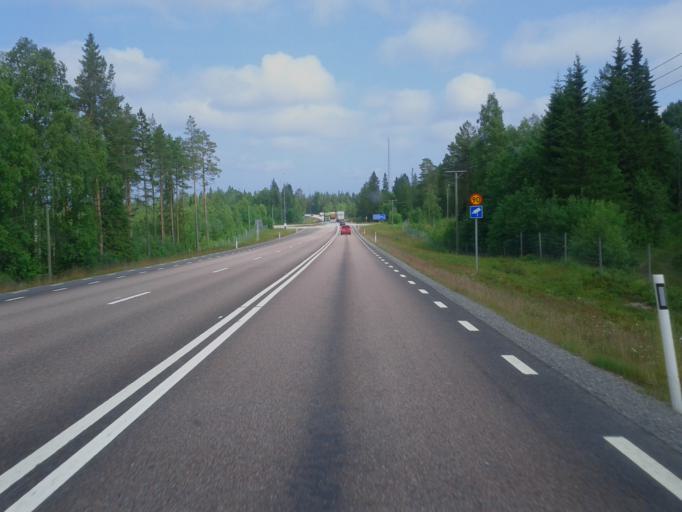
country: SE
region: Vaesterbotten
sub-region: Skelleftea Kommun
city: Burea
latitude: 64.4630
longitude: 21.2918
